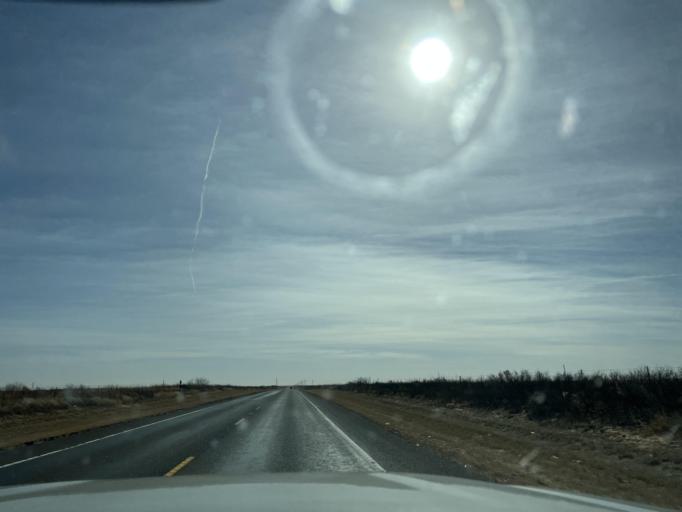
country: US
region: Texas
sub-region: Andrews County
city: Andrews
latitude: 32.4292
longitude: -102.4371
